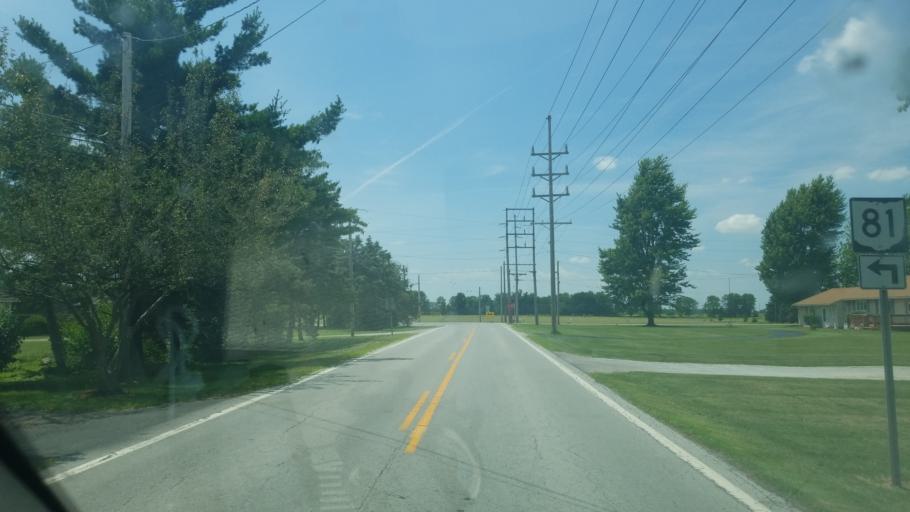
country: US
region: Ohio
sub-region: Hancock County
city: Arlington
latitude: 40.7831
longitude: -83.6506
